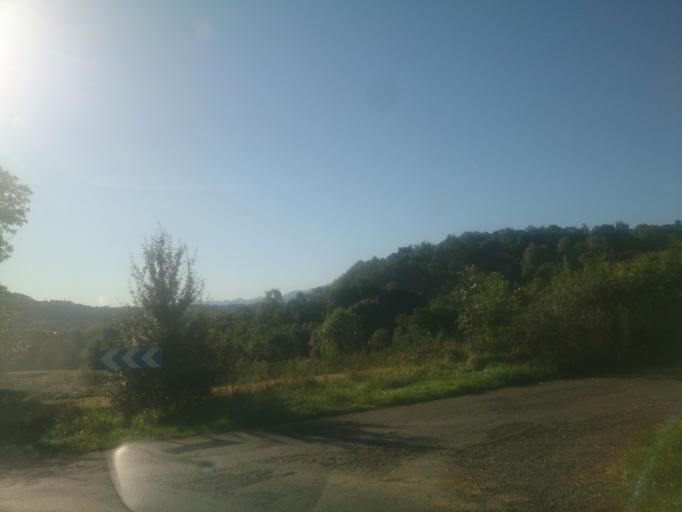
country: FR
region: Midi-Pyrenees
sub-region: Departement des Hautes-Pyrenees
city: Horgues
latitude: 43.1335
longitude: 0.0973
